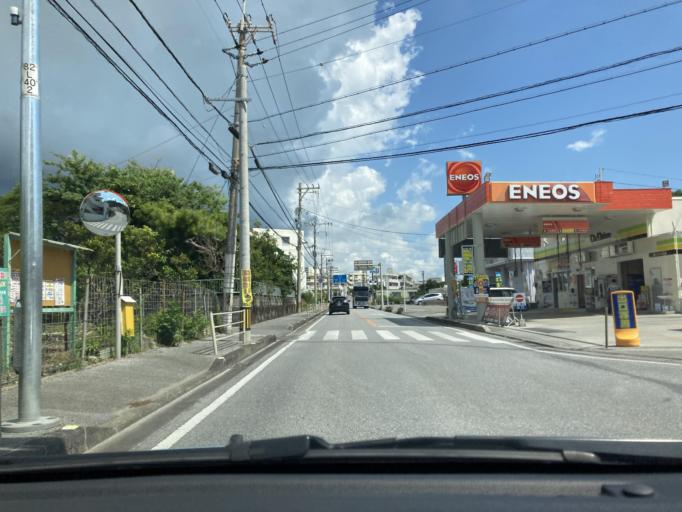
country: JP
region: Okinawa
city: Tomigusuku
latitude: 26.1838
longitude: 127.7261
